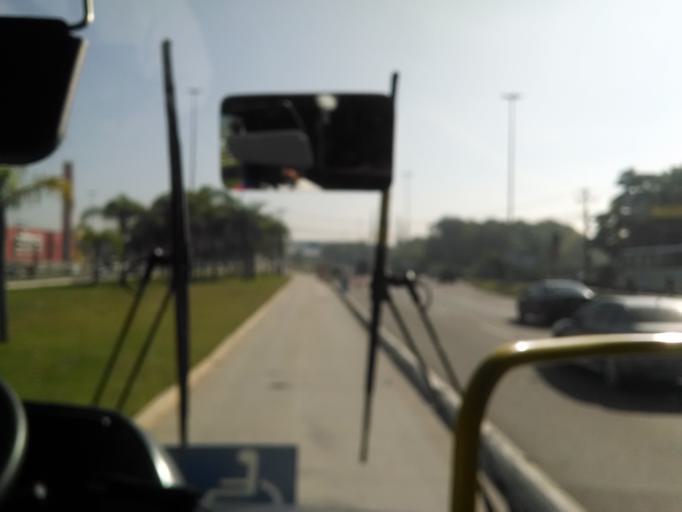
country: BR
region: Rio de Janeiro
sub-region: Rio De Janeiro
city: Rio de Janeiro
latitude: -22.9824
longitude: -43.3655
